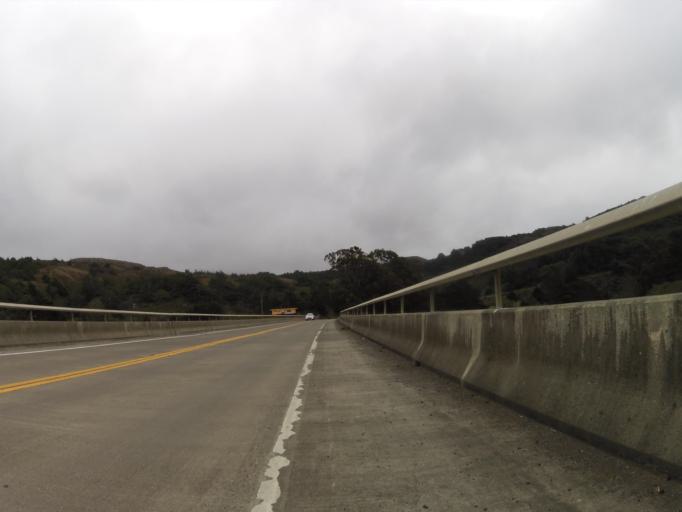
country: US
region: California
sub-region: Sonoma County
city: Monte Rio
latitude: 38.4351
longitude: -123.1021
